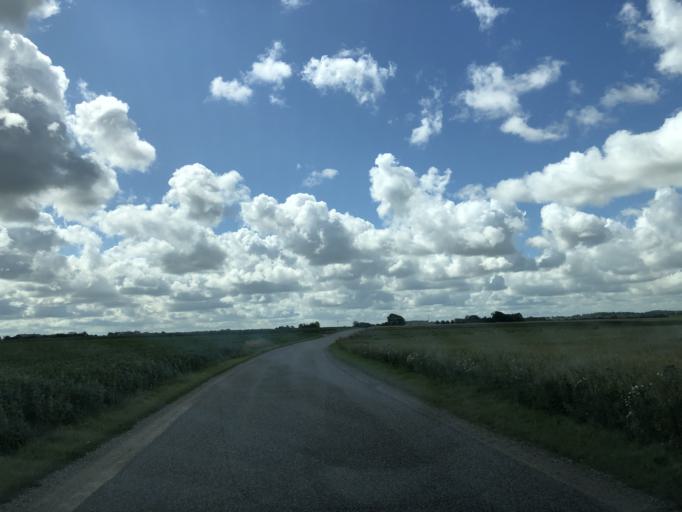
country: DK
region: Central Jutland
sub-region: Struer Kommune
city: Struer
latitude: 56.4550
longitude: 8.5240
